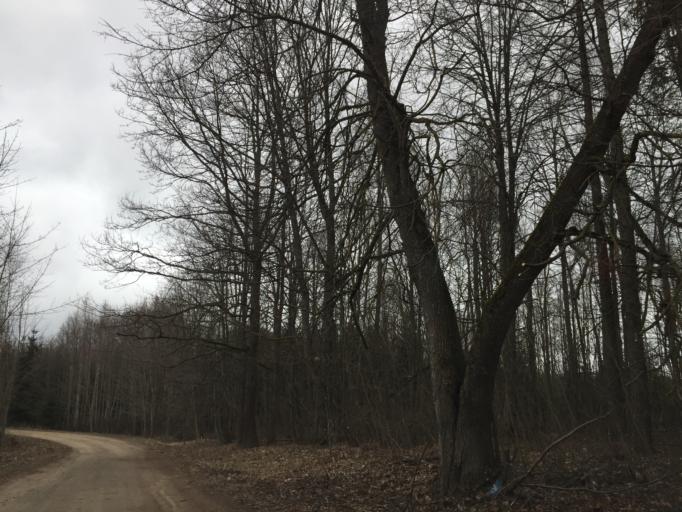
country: LV
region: Ilukste
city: Ilukste
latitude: 55.9071
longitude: 26.3651
